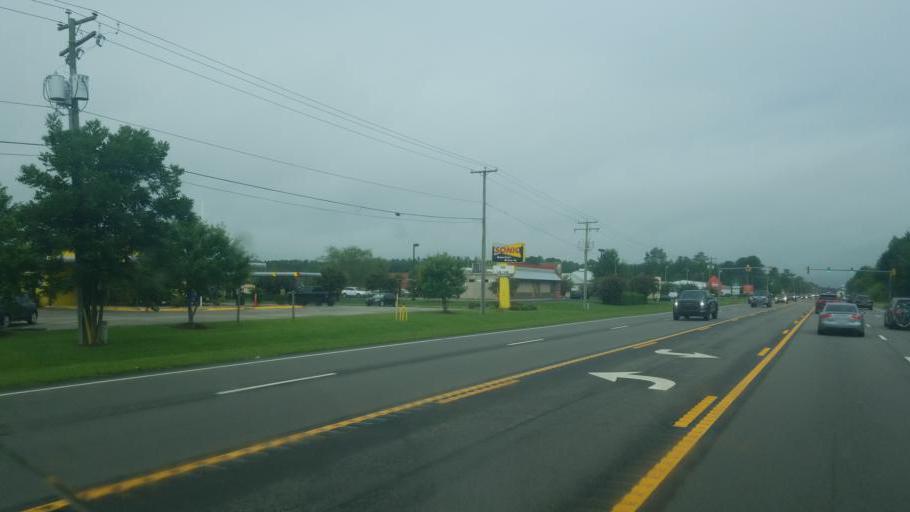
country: US
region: North Carolina
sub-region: Currituck County
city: Moyock
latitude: 36.5167
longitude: -76.1690
